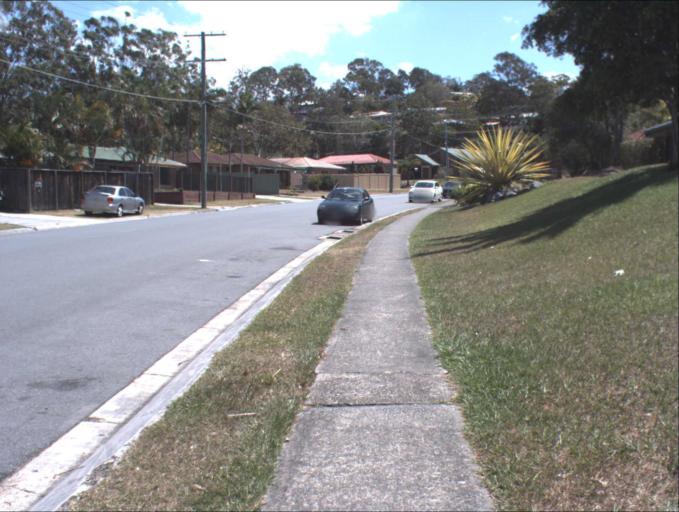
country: AU
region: Queensland
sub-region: Logan
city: Windaroo
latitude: -27.7317
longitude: 153.2059
